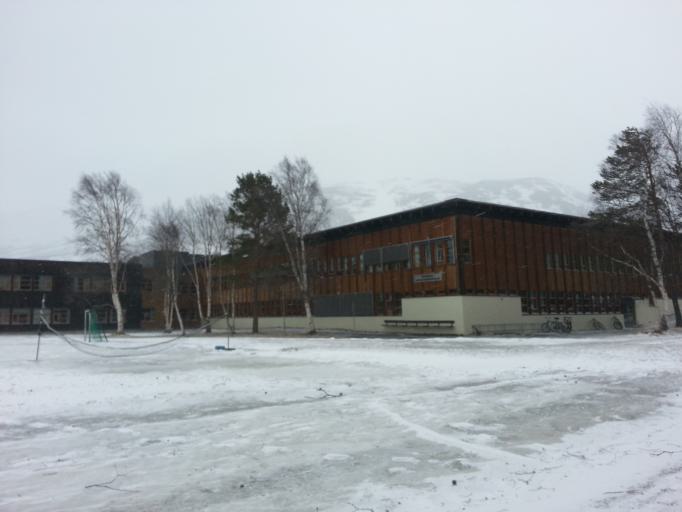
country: NO
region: Sor-Trondelag
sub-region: Oppdal
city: Oppdal
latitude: 62.5953
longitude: 9.6859
